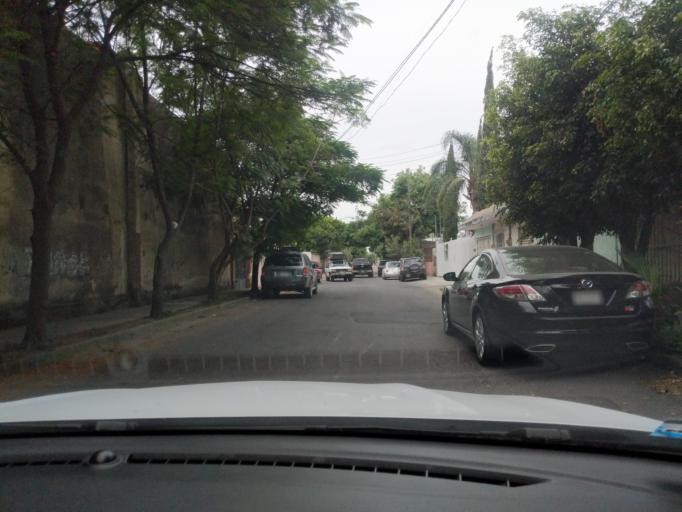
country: MX
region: Jalisco
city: Nuevo Mexico
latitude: 20.7598
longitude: -103.4381
